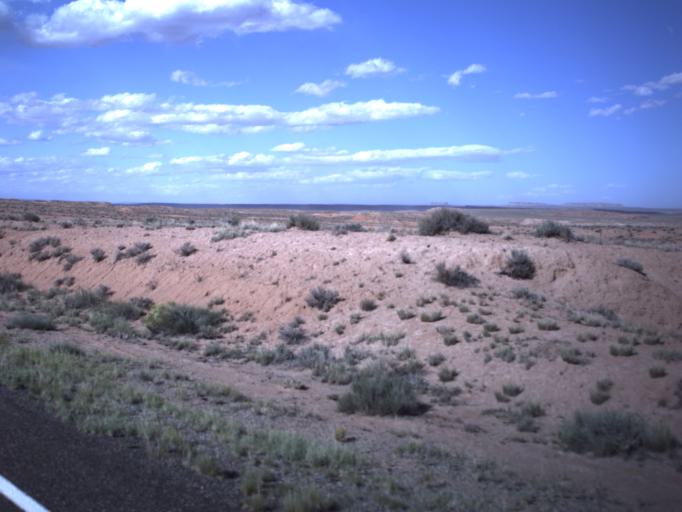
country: US
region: Utah
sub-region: Emery County
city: Ferron
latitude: 38.3003
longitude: -110.6688
